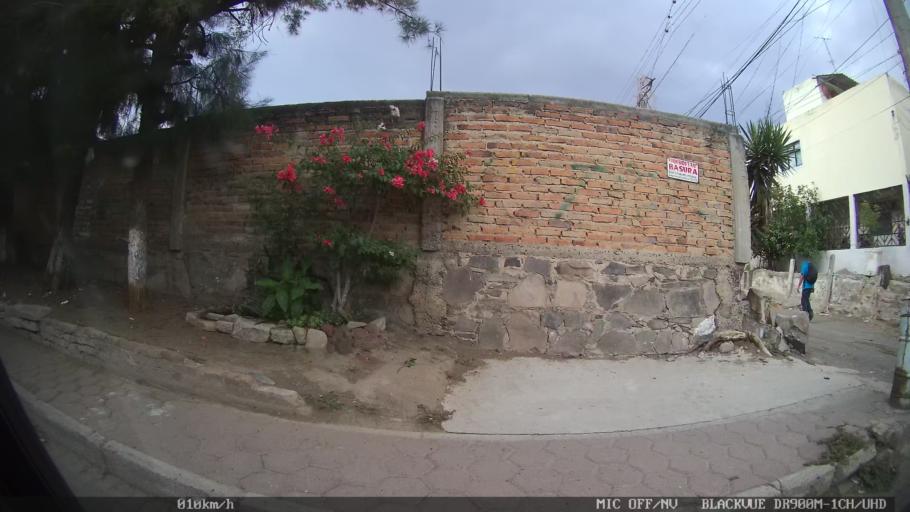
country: MX
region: Jalisco
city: Tonala
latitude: 20.6229
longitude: -103.2654
